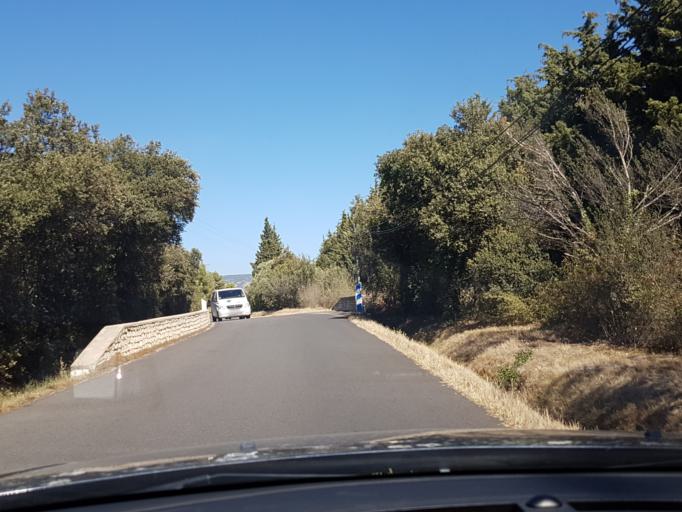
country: FR
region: Provence-Alpes-Cote d'Azur
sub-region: Departement des Bouches-du-Rhone
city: Orgon
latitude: 43.7841
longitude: 5.0188
